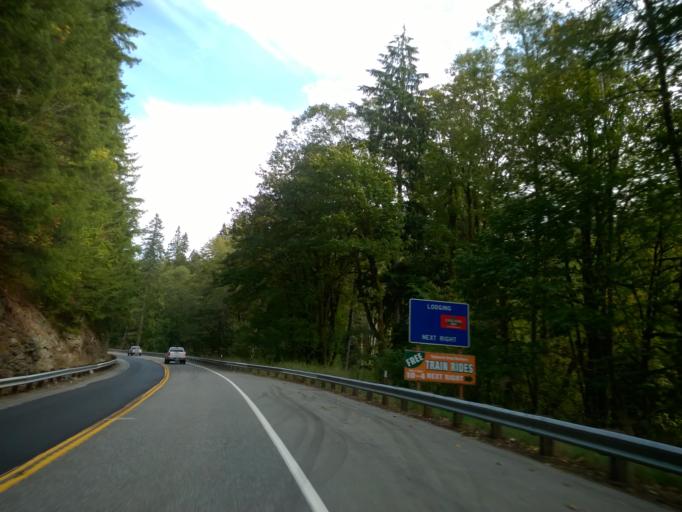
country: US
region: Washington
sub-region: Snohomish County
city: Gold Bar
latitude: 47.7104
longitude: -121.3697
